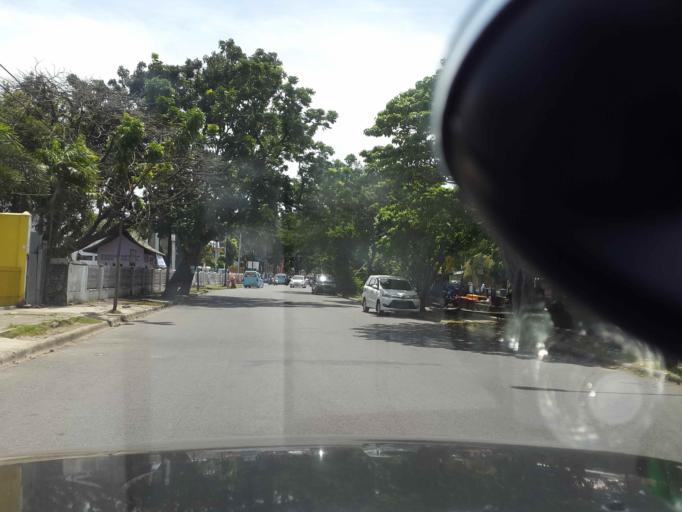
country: ID
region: West Sumatra
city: Padang
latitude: -0.9380
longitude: 100.3660
